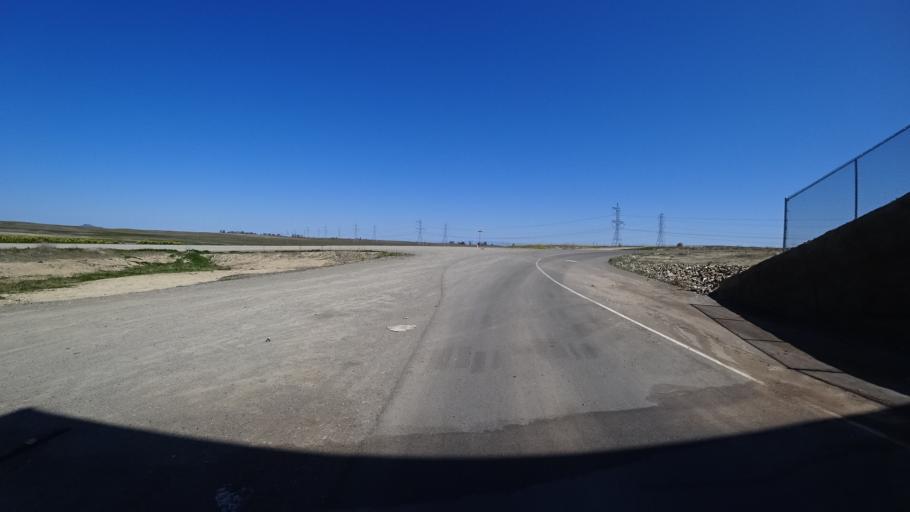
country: US
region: California
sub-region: Glenn County
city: Willows
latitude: 39.6328
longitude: -122.2765
